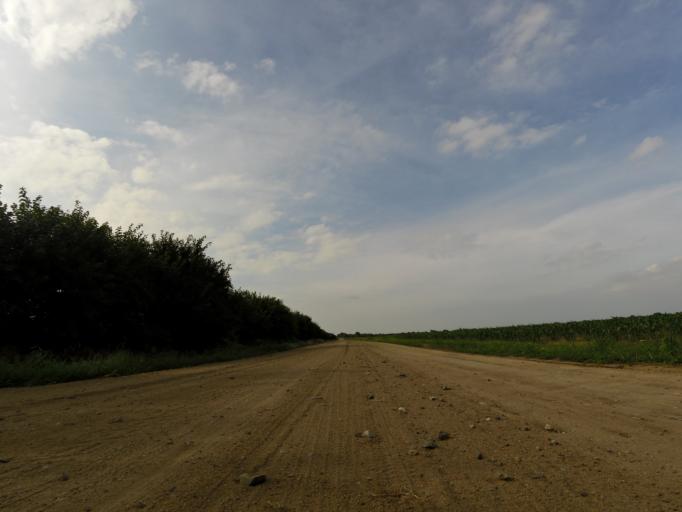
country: US
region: Kansas
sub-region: Reno County
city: South Hutchinson
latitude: 37.9785
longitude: -98.0687
